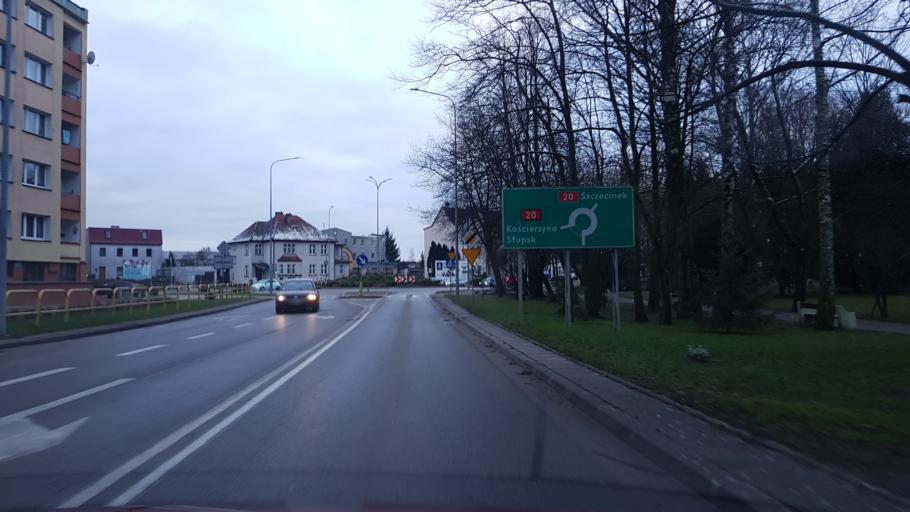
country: PL
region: Pomeranian Voivodeship
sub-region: Powiat bytowski
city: Miastko
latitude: 53.9999
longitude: 16.9759
